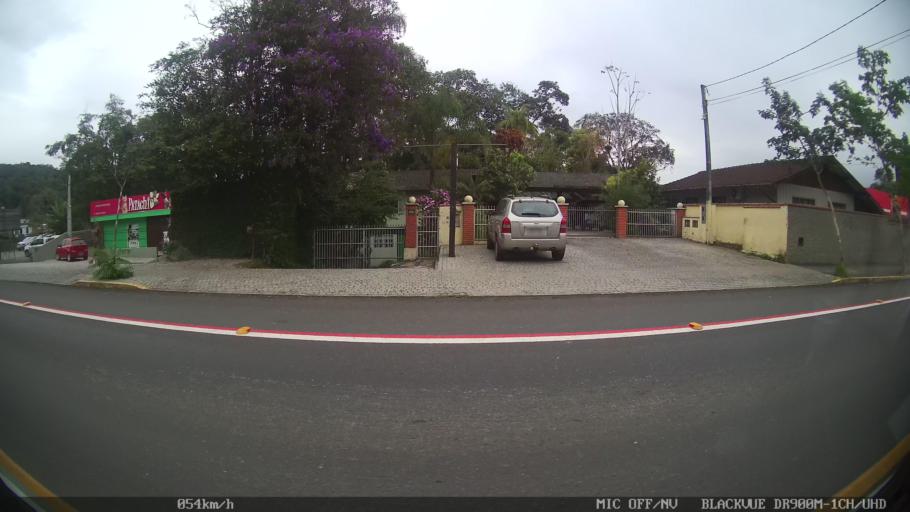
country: BR
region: Santa Catarina
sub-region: Joinville
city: Joinville
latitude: -26.2987
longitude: -48.8645
